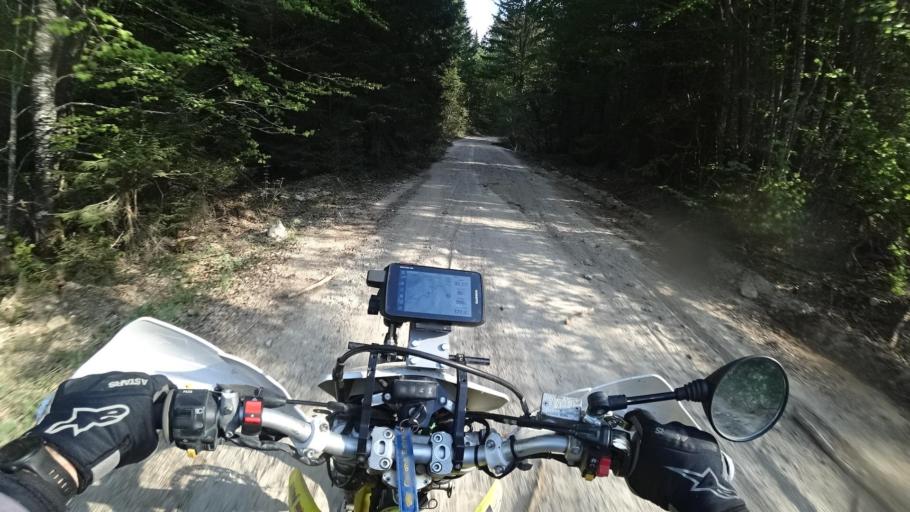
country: BA
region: Federation of Bosnia and Herzegovina
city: Glamoc
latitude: 44.0678
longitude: 16.7706
